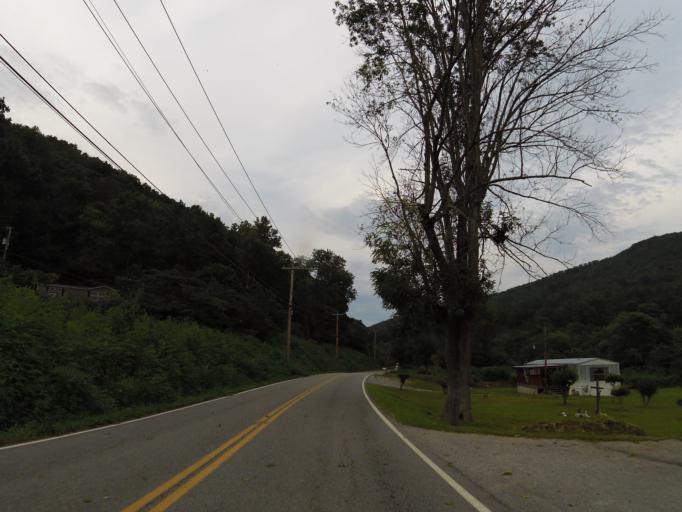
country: US
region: Tennessee
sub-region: Anderson County
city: Rocky Top
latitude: 36.2017
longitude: -84.1695
